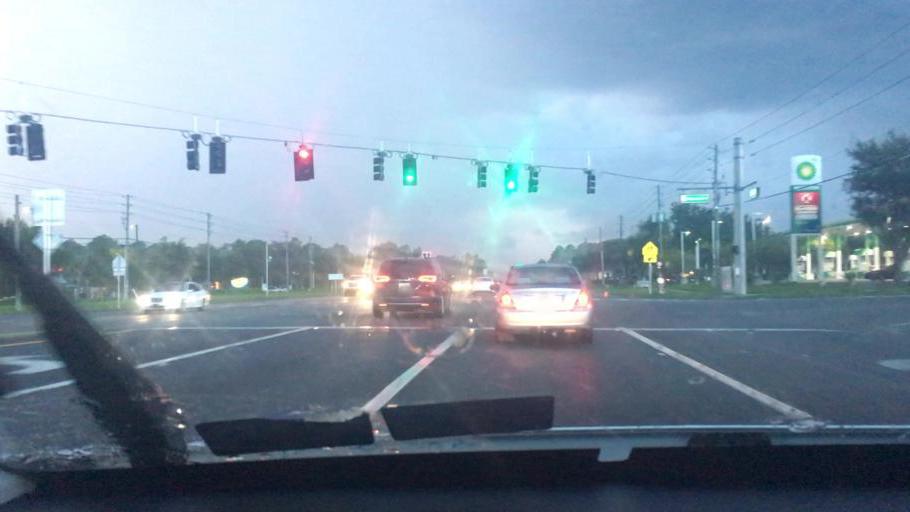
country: US
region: Florida
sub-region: Orange County
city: Bithlo
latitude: 28.5606
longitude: -81.1293
